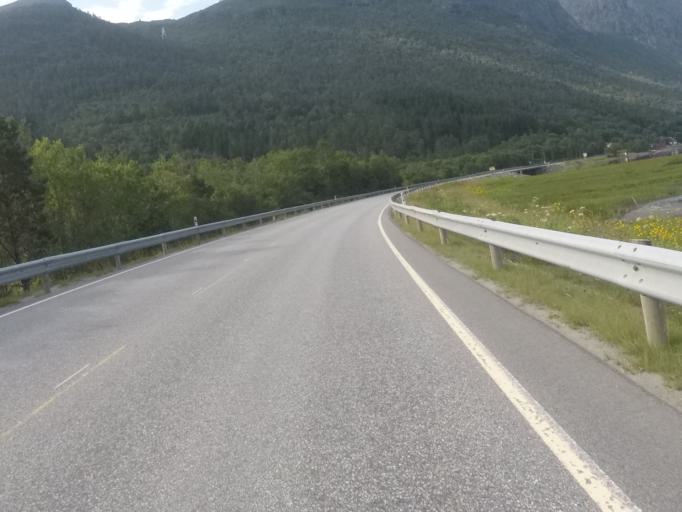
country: NO
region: More og Romsdal
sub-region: Rauma
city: Andalsnes
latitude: 62.5733
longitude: 7.7884
